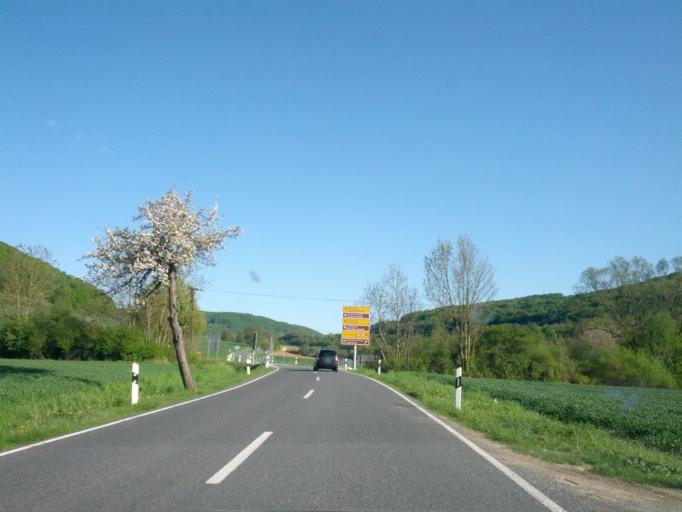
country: DE
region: Thuringia
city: Geismar
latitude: 51.2247
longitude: 10.1860
